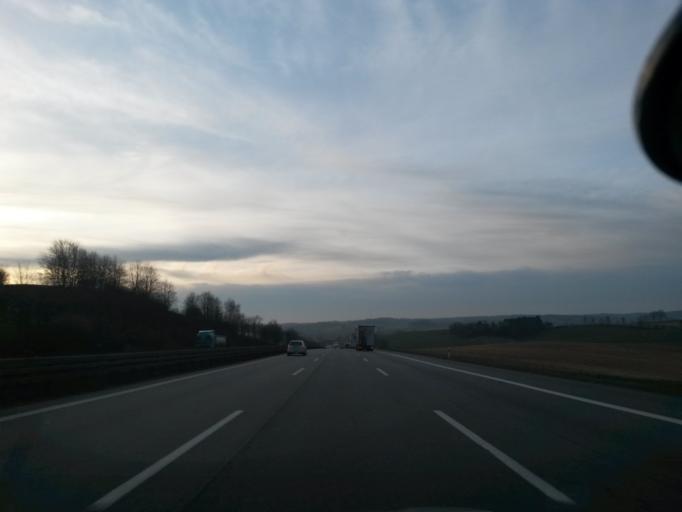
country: DE
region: Bavaria
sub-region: Upper Bavaria
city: Rohrbach
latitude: 48.6046
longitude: 11.5499
